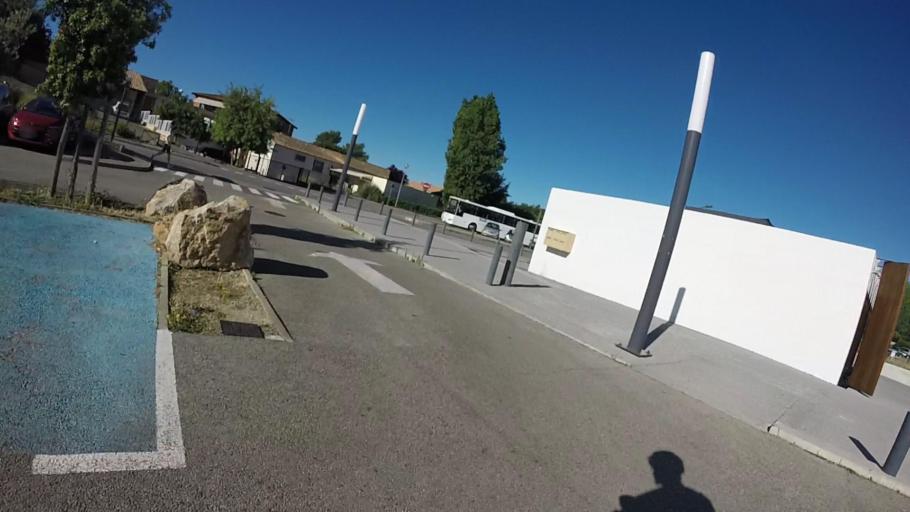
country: FR
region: Provence-Alpes-Cote d'Azur
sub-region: Departement des Alpes-Maritimes
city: Biot
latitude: 43.6231
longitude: 7.0517
